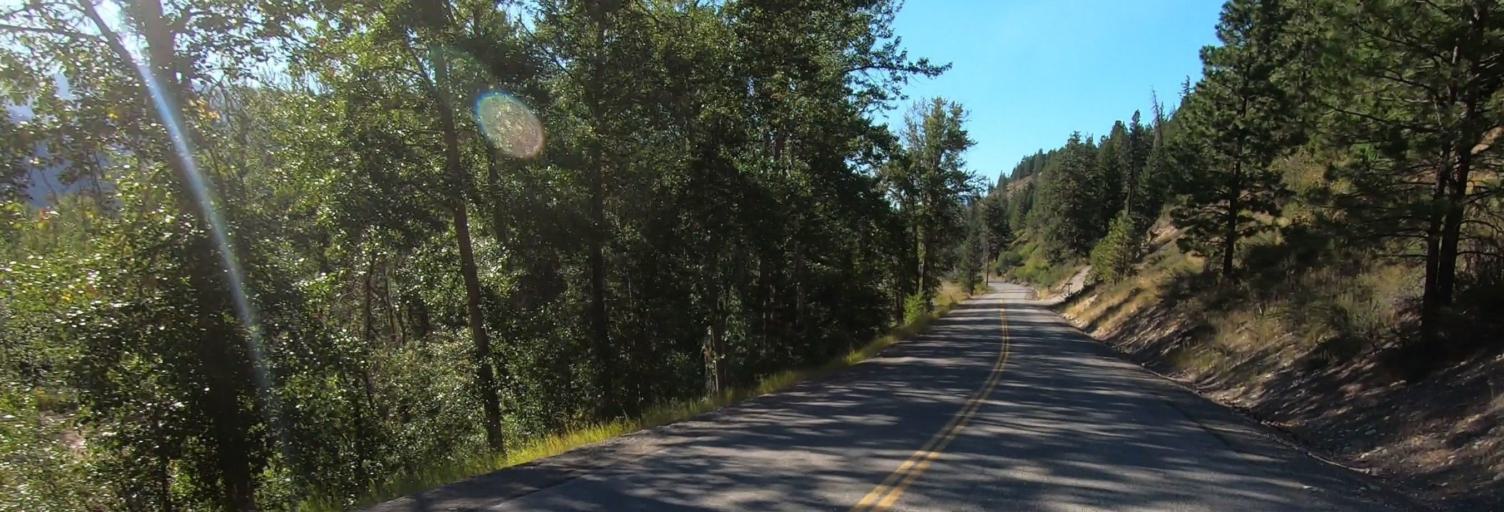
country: US
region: Washington
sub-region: Chelan County
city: Granite Falls
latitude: 48.5630
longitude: -120.3493
